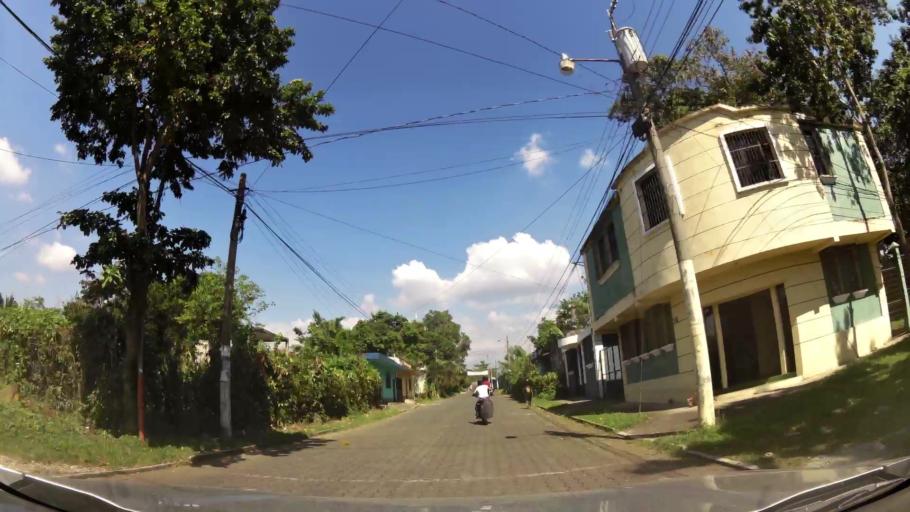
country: GT
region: Suchitepeque
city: Mazatenango
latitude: 14.5304
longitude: -91.4823
